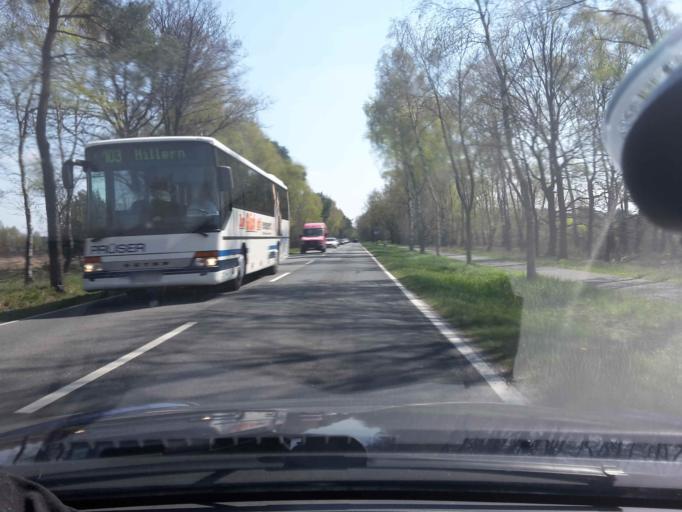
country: DE
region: Lower Saxony
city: Schneverdingen
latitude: 53.1034
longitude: 9.8287
